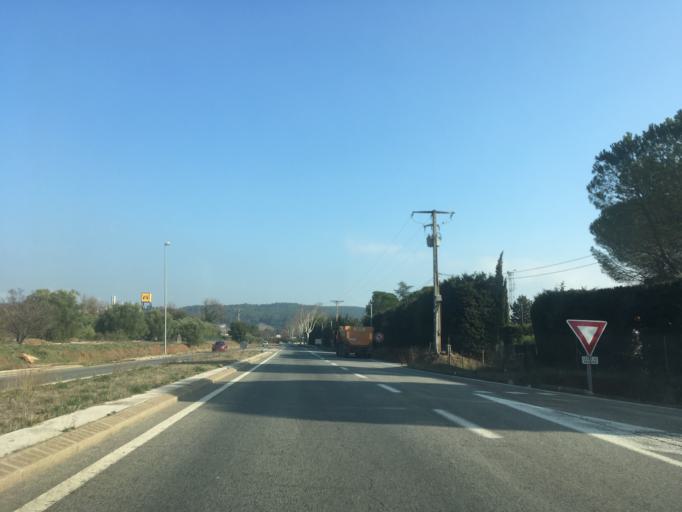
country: FR
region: Provence-Alpes-Cote d'Azur
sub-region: Departement du Var
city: Le Cannet-des-Maures
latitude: 43.3947
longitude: 6.3524
